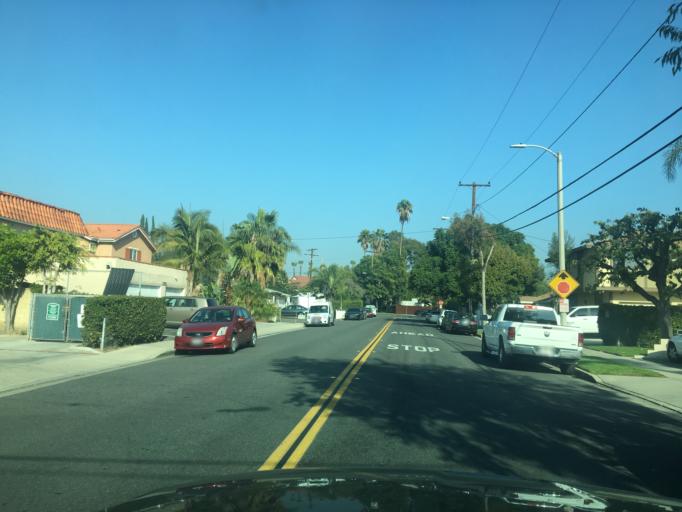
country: US
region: California
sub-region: Orange County
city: Tustin
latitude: 33.7355
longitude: -117.8268
